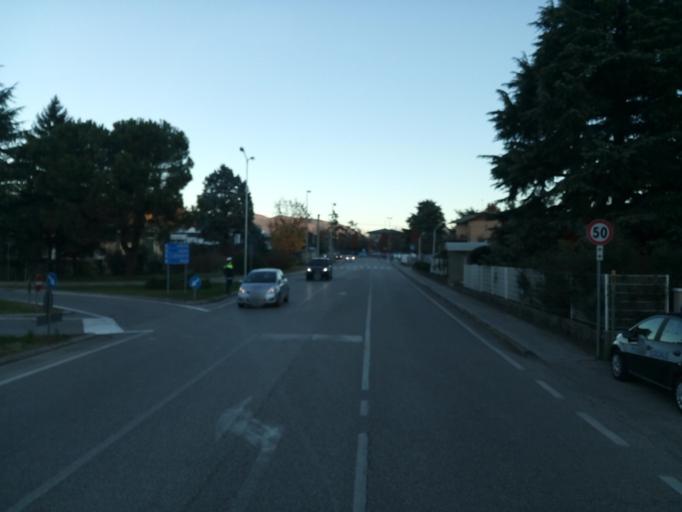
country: IT
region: Veneto
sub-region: Provincia di Vicenza
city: Trissino
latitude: 45.5601
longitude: 11.3790
